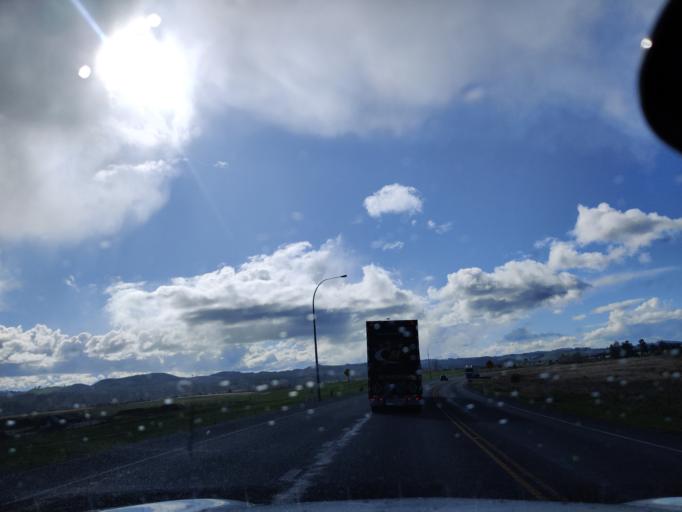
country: NZ
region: Waikato
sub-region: Taupo District
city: Taupo
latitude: -38.6666
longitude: 176.1014
